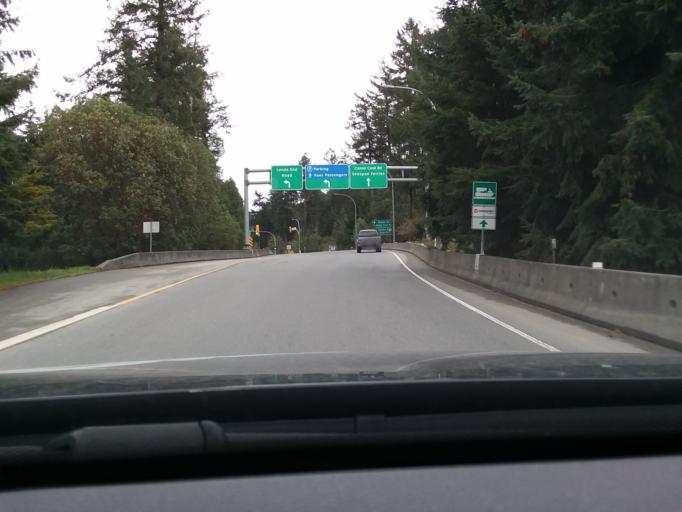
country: CA
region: British Columbia
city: North Saanich
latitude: 48.6826
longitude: -123.4136
